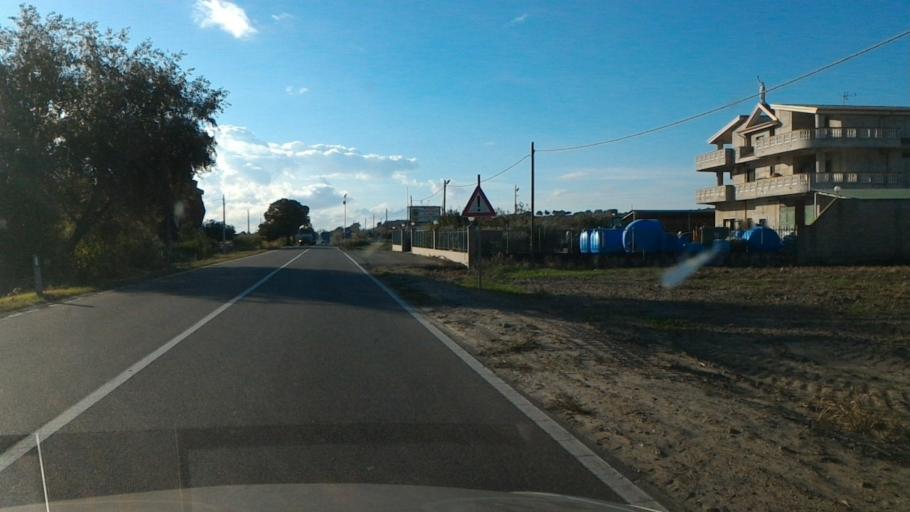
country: IT
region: Calabria
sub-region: Provincia di Crotone
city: Tronca
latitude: 39.2192
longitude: 17.1047
